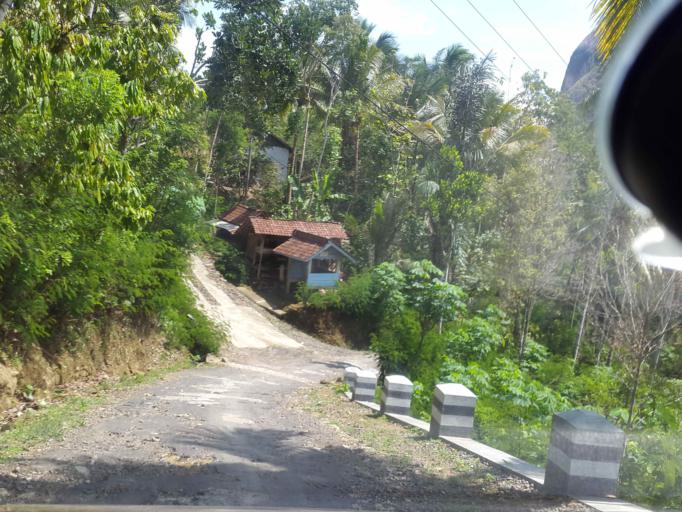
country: ID
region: East Java
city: Tawang
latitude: -8.1130
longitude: 111.5916
